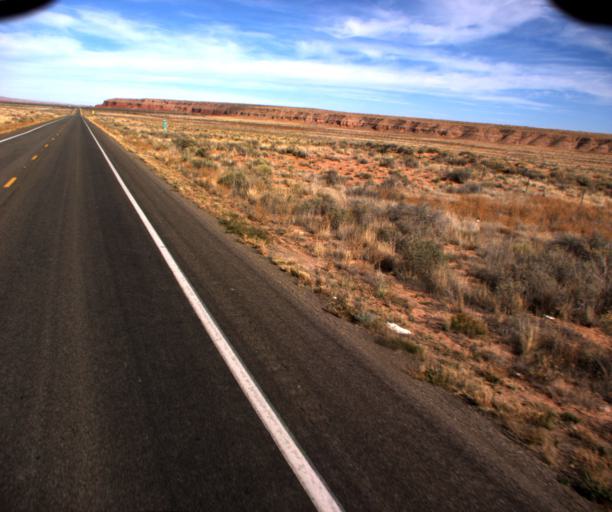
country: US
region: Arizona
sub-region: Navajo County
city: Kayenta
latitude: 36.7470
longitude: -110.0687
